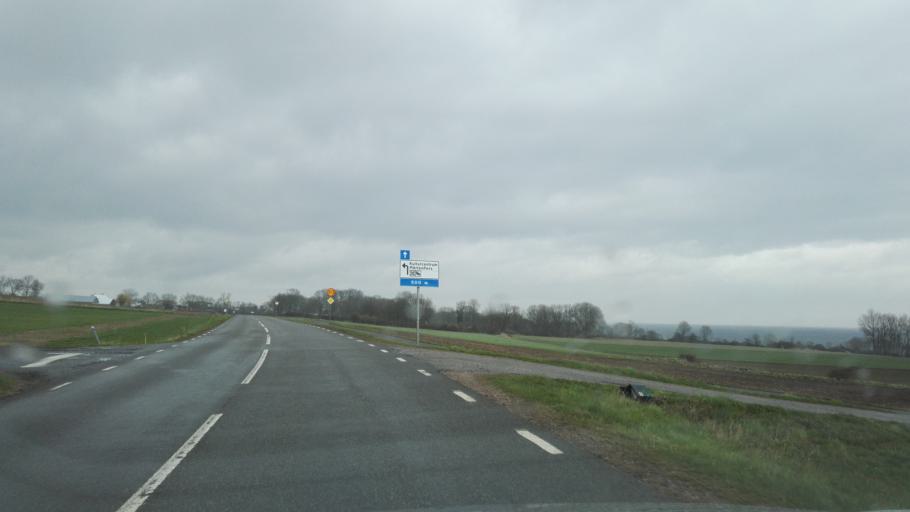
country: SE
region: Skane
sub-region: Simrishamns Kommun
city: Simrishamn
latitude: 55.4930
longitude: 14.3127
